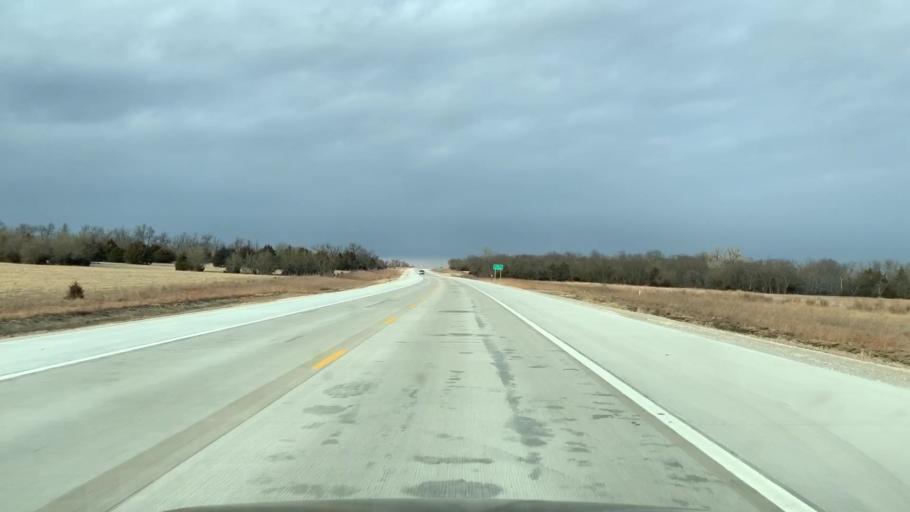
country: US
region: Kansas
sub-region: Allen County
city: Iola
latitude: 37.8645
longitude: -95.4034
